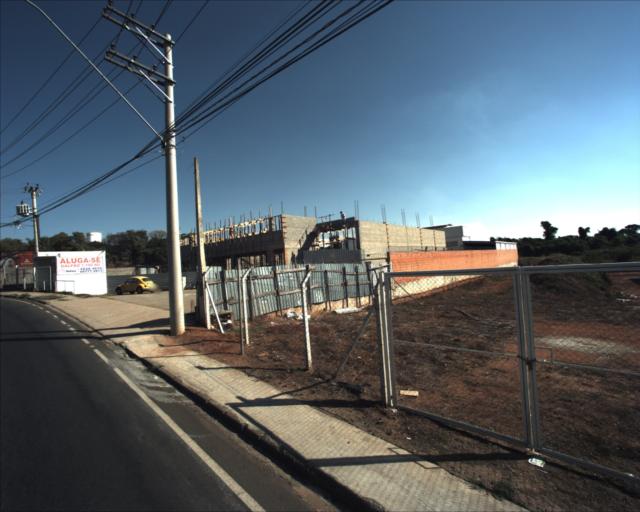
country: BR
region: Sao Paulo
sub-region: Sorocaba
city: Sorocaba
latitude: -23.4542
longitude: -47.4187
